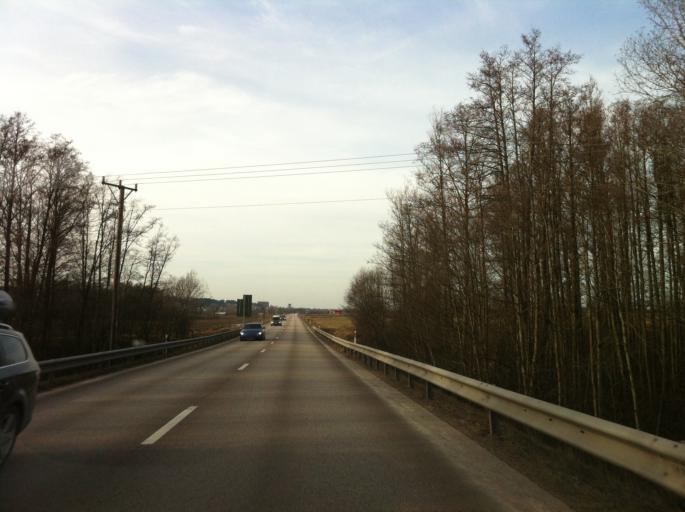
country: SE
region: Vaermland
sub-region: Kristinehamns Kommun
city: Kristinehamn
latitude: 59.2861
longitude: 14.1422
